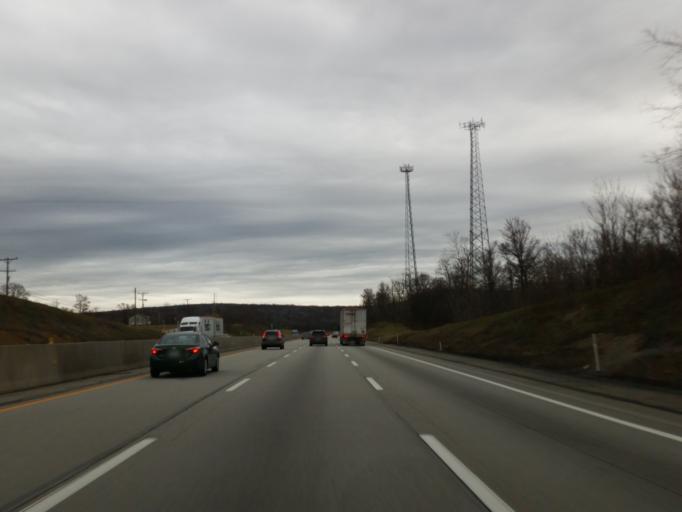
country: US
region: Pennsylvania
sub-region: Westmoreland County
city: Ligonier
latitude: 40.1284
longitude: -79.2894
